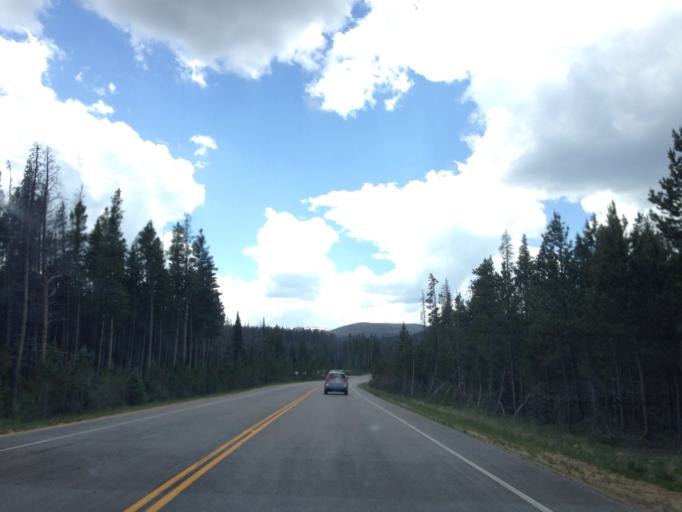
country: US
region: Colorado
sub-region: Larimer County
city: Estes Park
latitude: 40.5833
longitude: -105.8504
